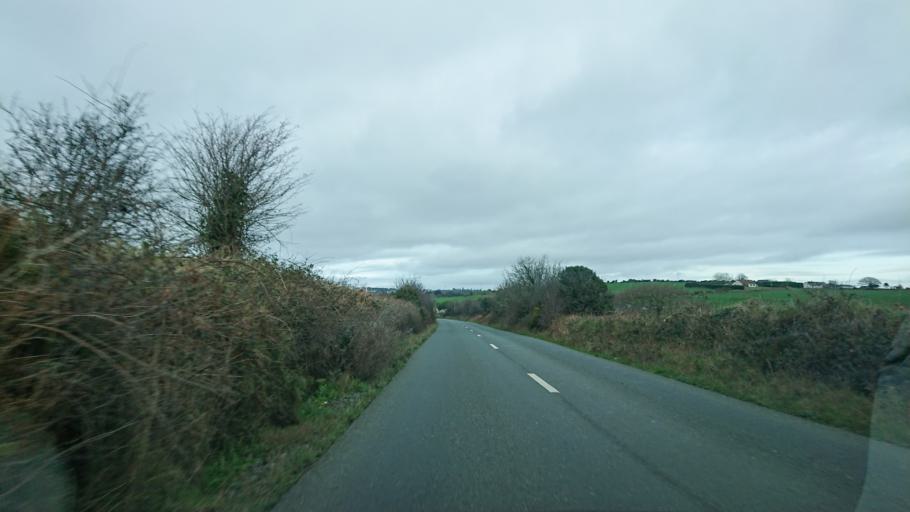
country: IE
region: Leinster
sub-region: Kilkenny
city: Mooncoin
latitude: 52.2155
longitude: -7.2406
